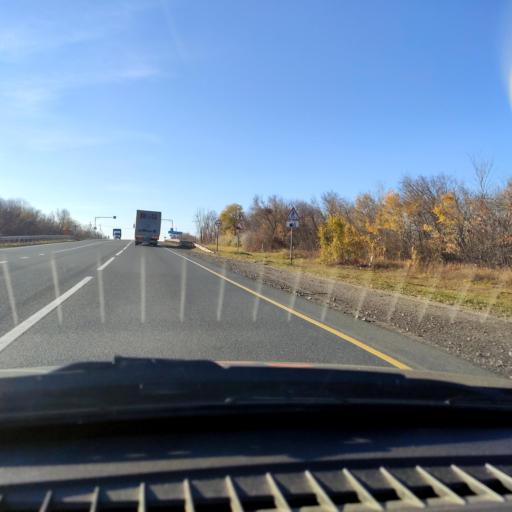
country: RU
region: Samara
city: Mezhdurechensk
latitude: 53.2560
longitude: 49.1338
